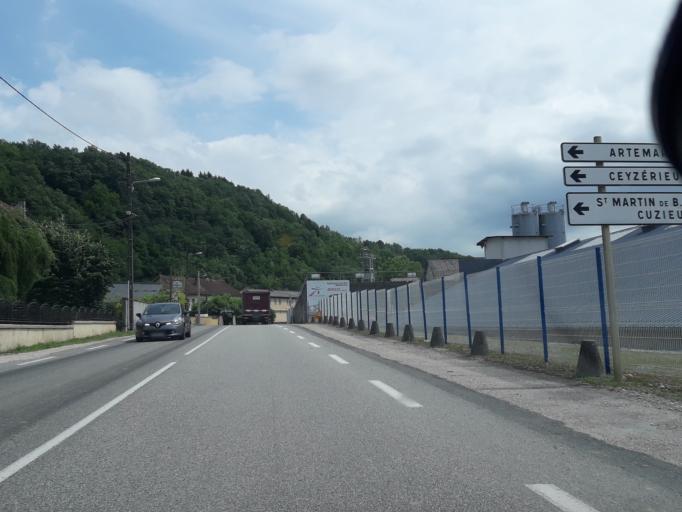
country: FR
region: Rhone-Alpes
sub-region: Departement de l'Ain
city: Belley
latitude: 45.8073
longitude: 5.6820
